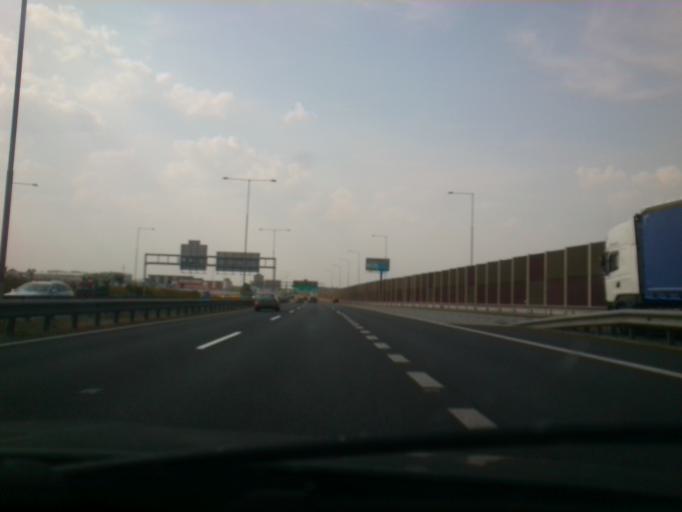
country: CZ
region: Central Bohemia
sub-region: Okres Praha-Zapad
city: Pruhonice
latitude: 49.9852
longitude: 14.6011
